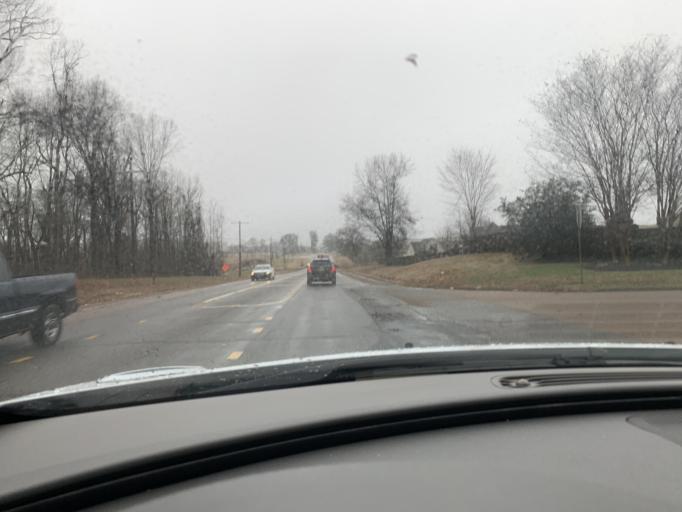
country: US
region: Mississippi
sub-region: De Soto County
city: Horn Lake
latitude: 34.9194
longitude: -90.0066
